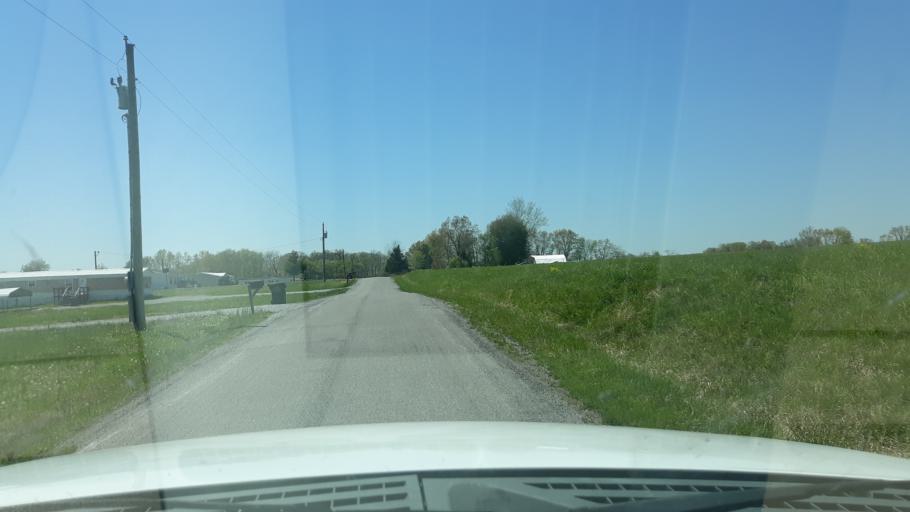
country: US
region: Illinois
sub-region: Saline County
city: Harrisburg
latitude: 37.8849
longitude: -88.6569
